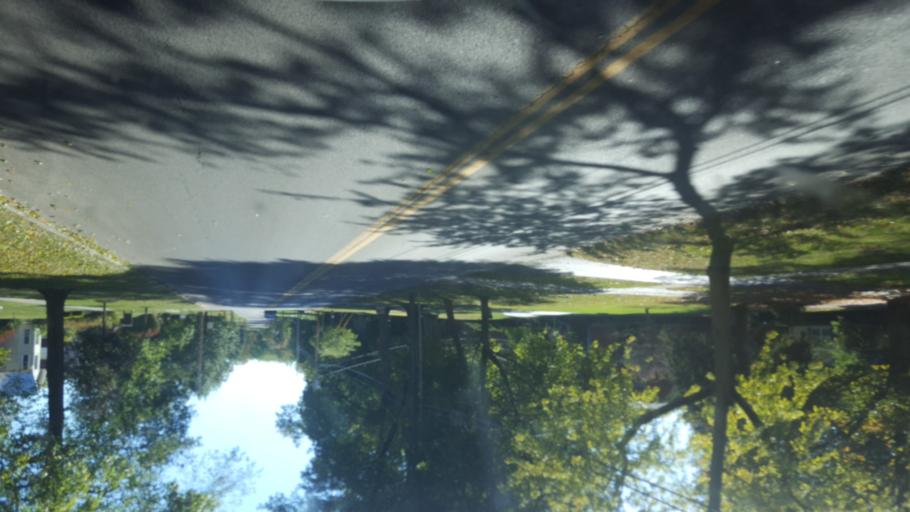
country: US
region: Ohio
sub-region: Wyandot County
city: Upper Sandusky
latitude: 40.8210
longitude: -83.2814
